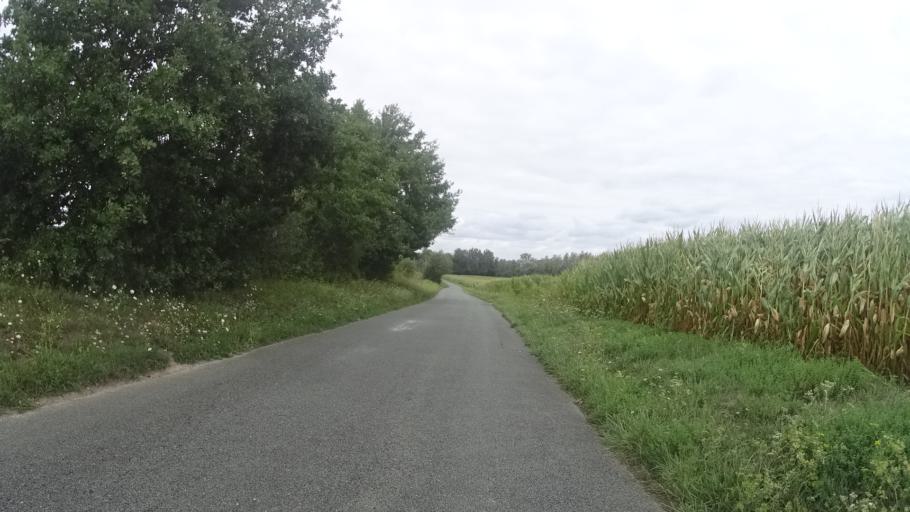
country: FR
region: Picardie
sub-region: Departement de l'Oise
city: Chiry-Ourscamp
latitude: 49.5193
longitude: 2.9500
